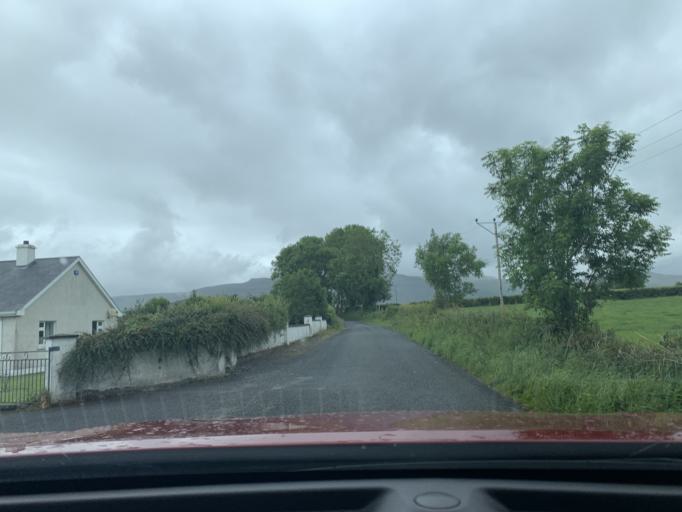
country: IE
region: Connaught
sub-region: Sligo
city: Sligo
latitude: 54.3066
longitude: -8.4554
